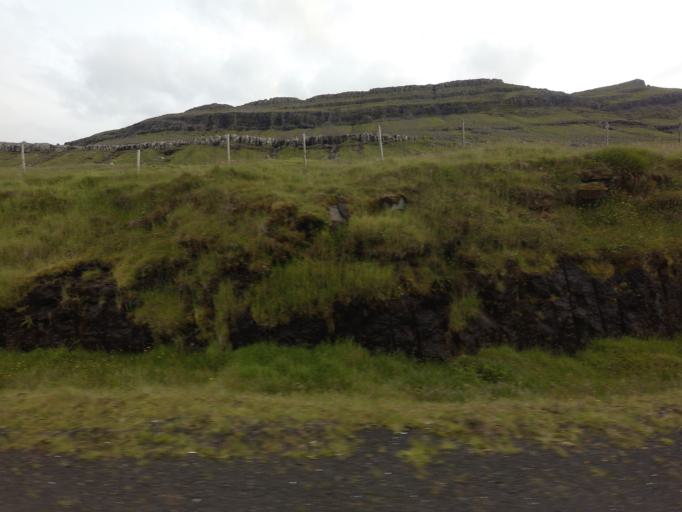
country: FO
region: Streymoy
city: Kollafjordhur
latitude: 62.1416
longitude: -6.8992
